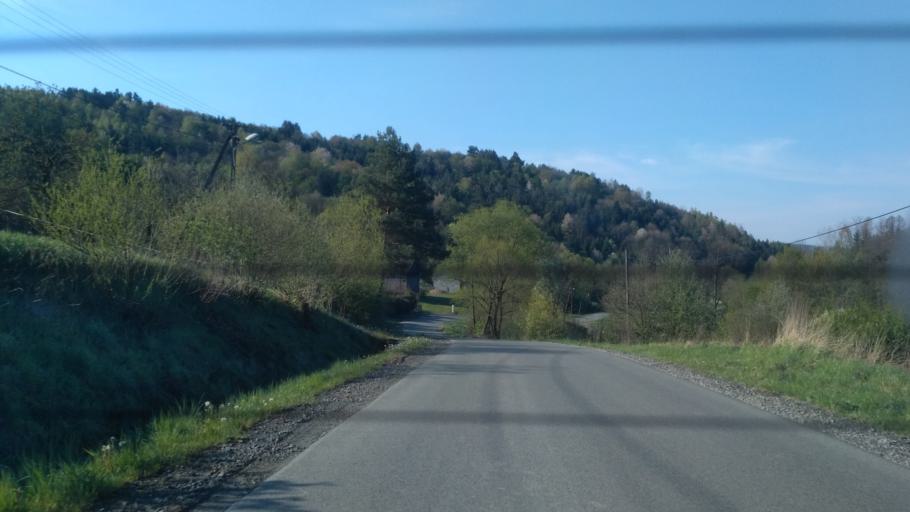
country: PL
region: Subcarpathian Voivodeship
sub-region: Powiat jaroslawski
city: Kramarzowka
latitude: 49.8210
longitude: 22.4957
